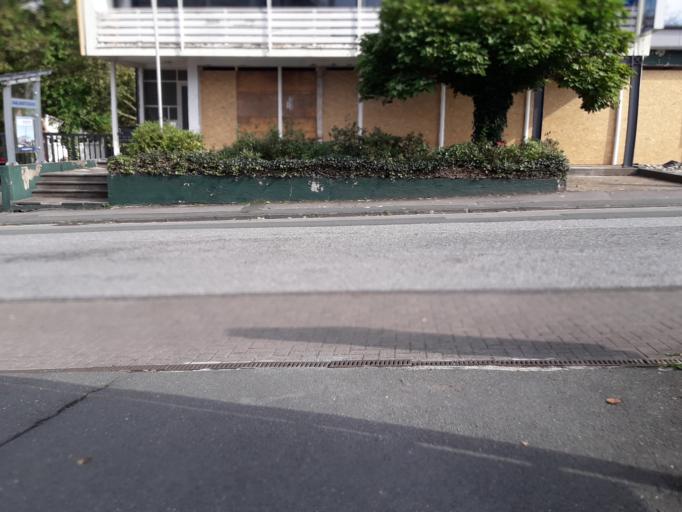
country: DE
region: North Rhine-Westphalia
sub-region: Regierungsbezirk Detmold
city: Paderborn
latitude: 51.7173
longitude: 8.7770
